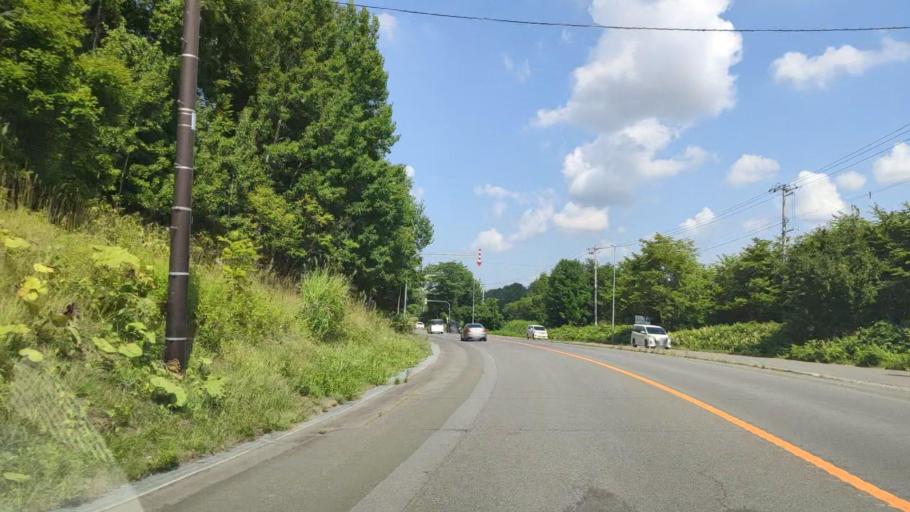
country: JP
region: Hokkaido
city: Shimo-furano
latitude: 43.5515
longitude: 142.4392
